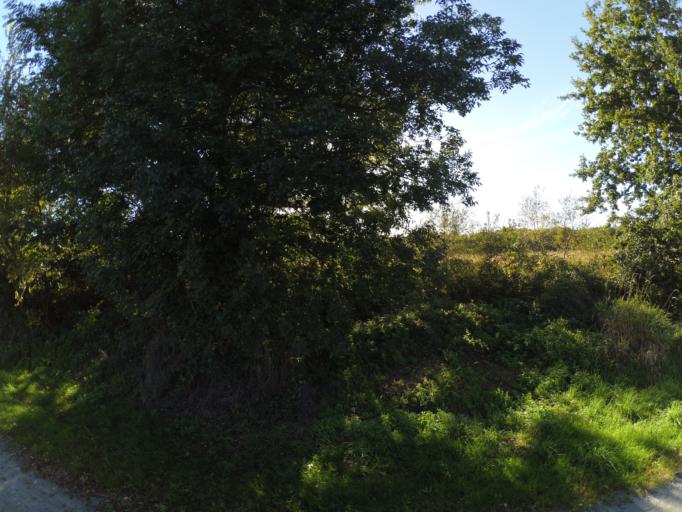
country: FR
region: Brittany
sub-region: Departement du Morbihan
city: Peillac
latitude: 47.7318
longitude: -2.2223
